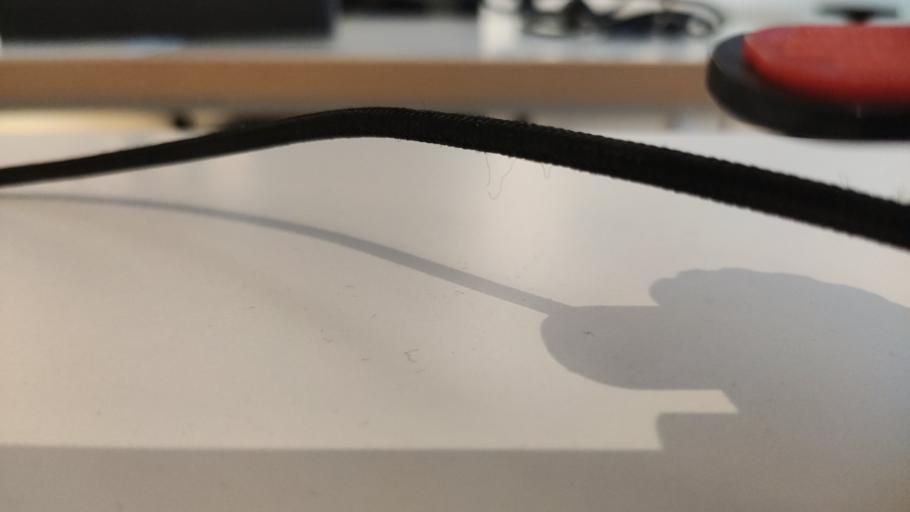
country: RU
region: Moskovskaya
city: Ruza
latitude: 55.8018
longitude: 36.2903
